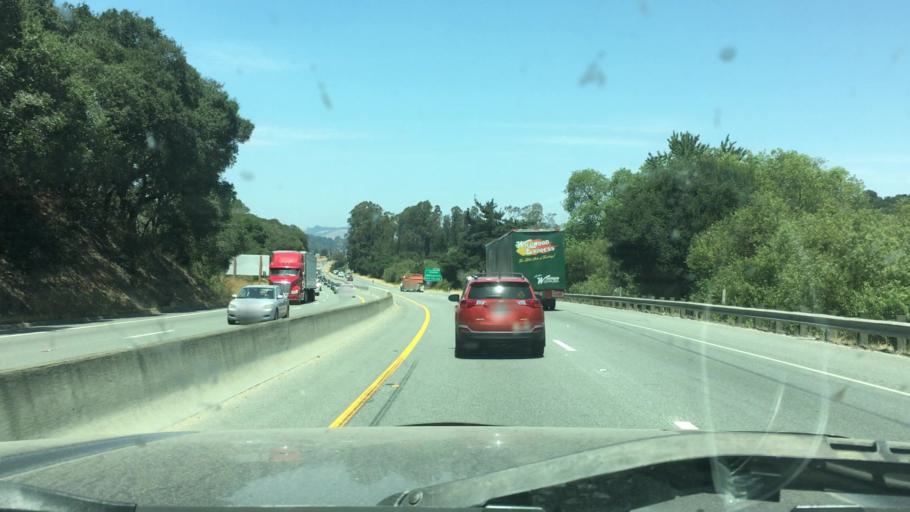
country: US
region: California
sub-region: San Benito County
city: Aromas
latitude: 36.8295
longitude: -121.6331
